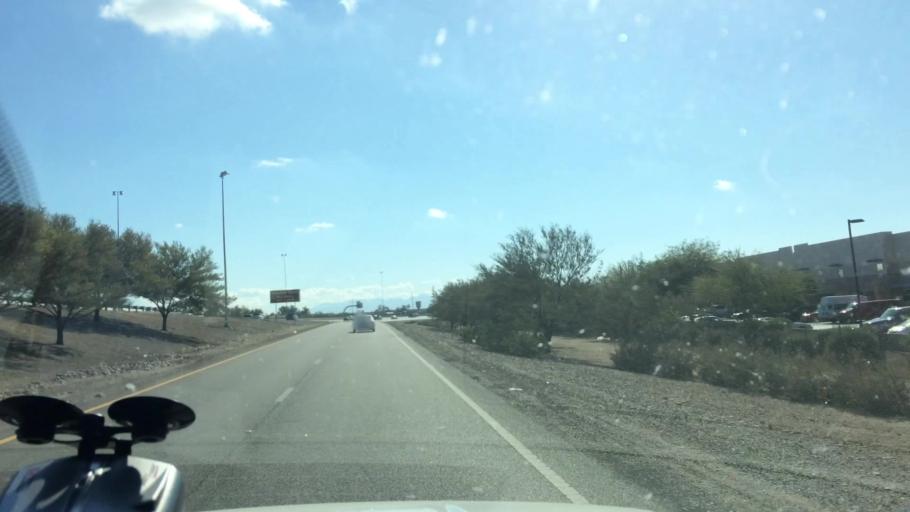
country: US
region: Arizona
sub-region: Maricopa County
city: Peoria
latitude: 33.5646
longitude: -112.2578
